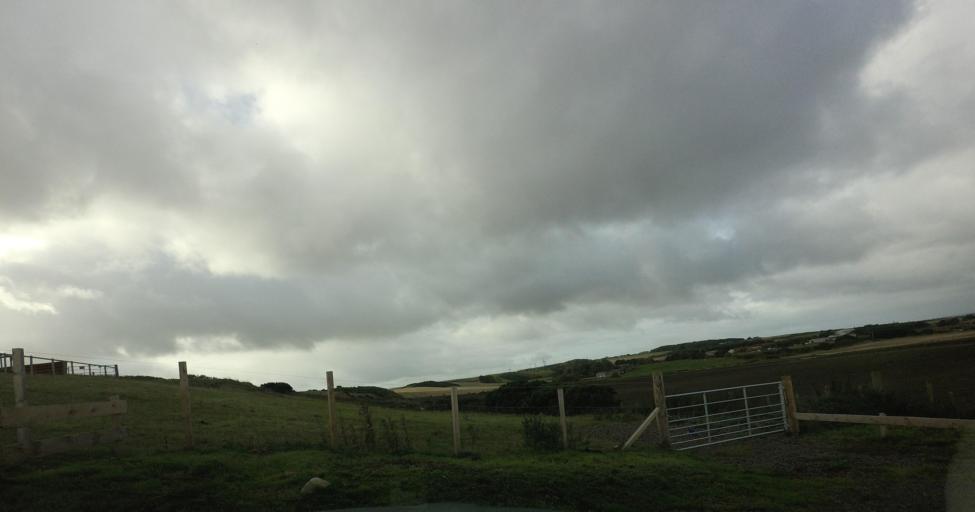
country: GB
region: Scotland
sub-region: Aberdeenshire
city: Banff
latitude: 57.6646
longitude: -2.5535
